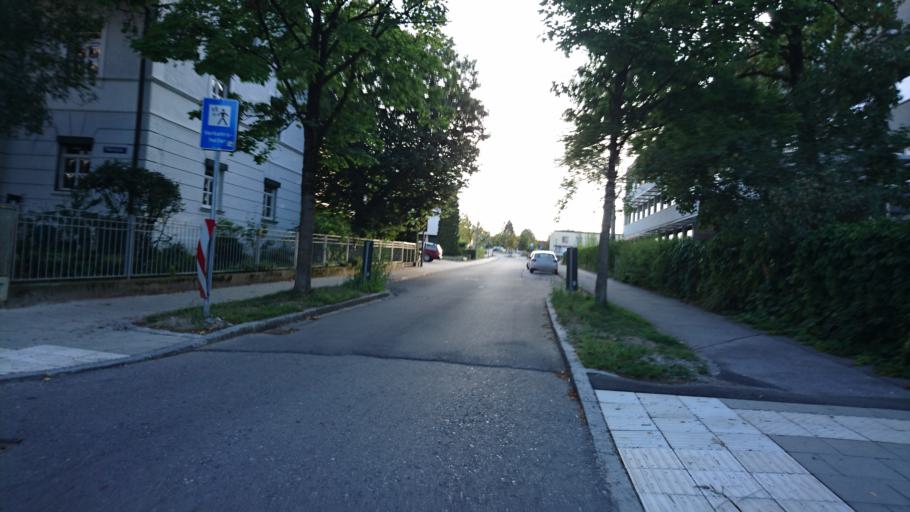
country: DE
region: Bavaria
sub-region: Upper Bavaria
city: Markt Schwaben
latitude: 48.1896
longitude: 11.8661
